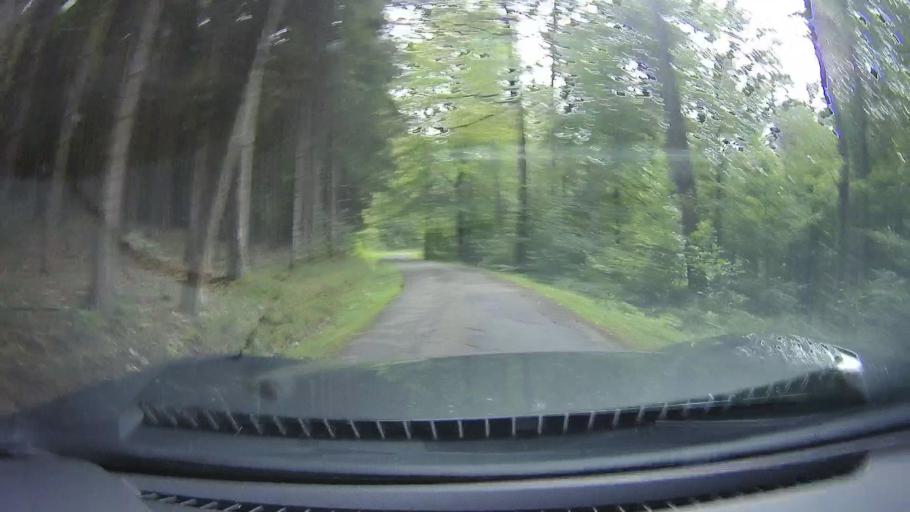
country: DE
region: Baden-Wuerttemberg
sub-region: Regierungsbezirk Stuttgart
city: Wustenrot
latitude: 49.0631
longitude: 9.4707
